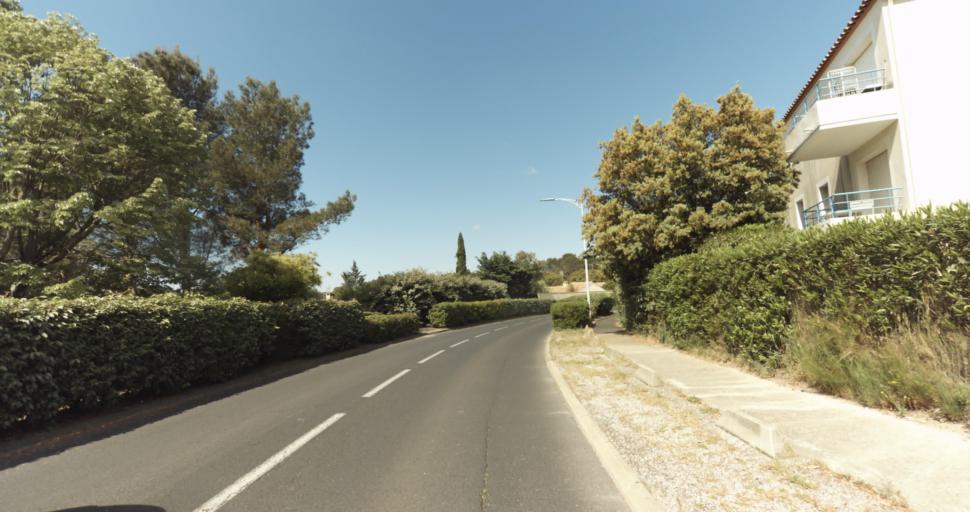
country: FR
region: Languedoc-Roussillon
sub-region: Departement du Gard
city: Nimes
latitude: 43.8507
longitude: 4.3136
